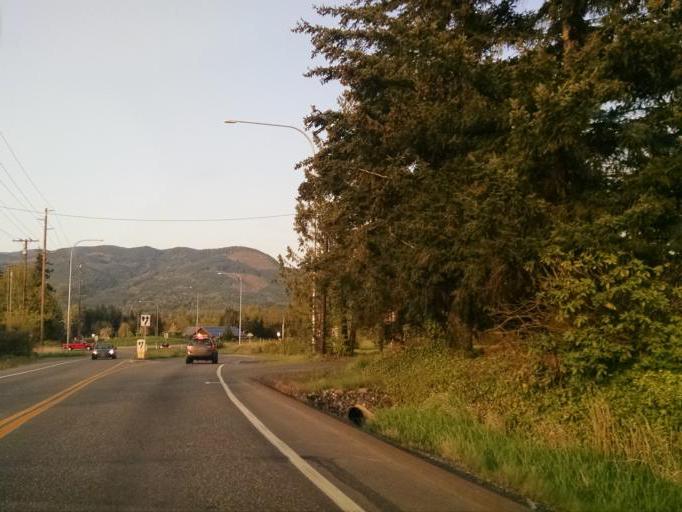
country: US
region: Washington
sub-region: Whatcom County
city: Everson
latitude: 48.8312
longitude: -122.3069
